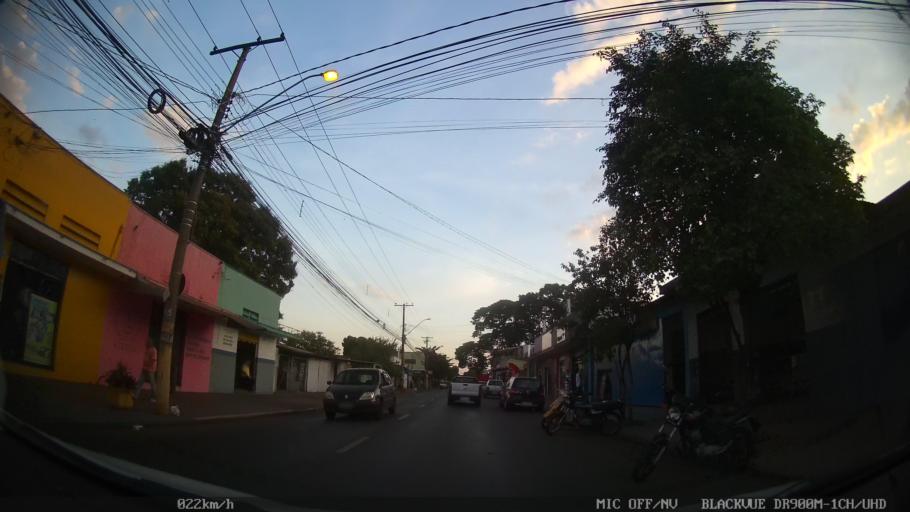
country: BR
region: Sao Paulo
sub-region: Ribeirao Preto
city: Ribeirao Preto
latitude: -21.1295
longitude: -47.8126
